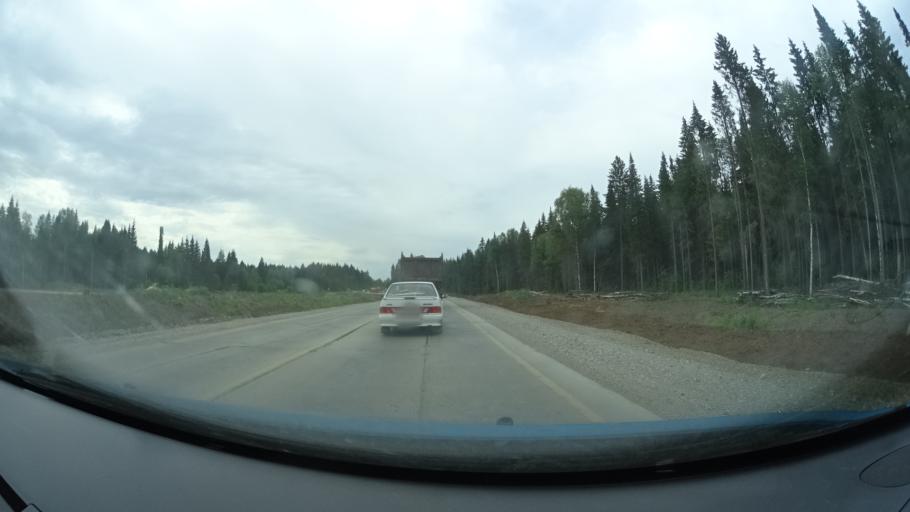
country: RU
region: Perm
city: Bershet'
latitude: 57.7018
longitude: 56.3861
